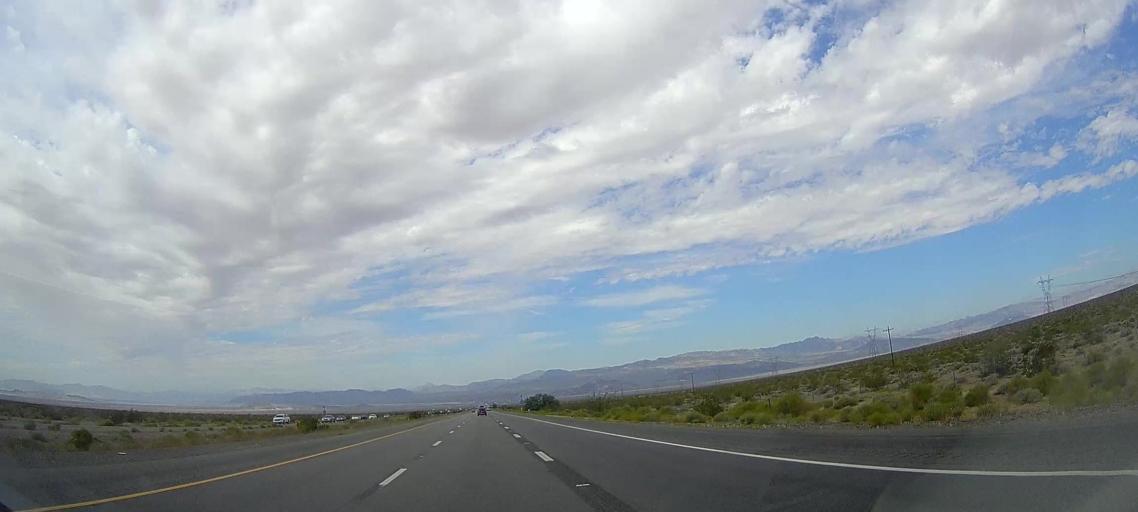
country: US
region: Nevada
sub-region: Clark County
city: Sandy Valley
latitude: 35.3351
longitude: -115.9651
